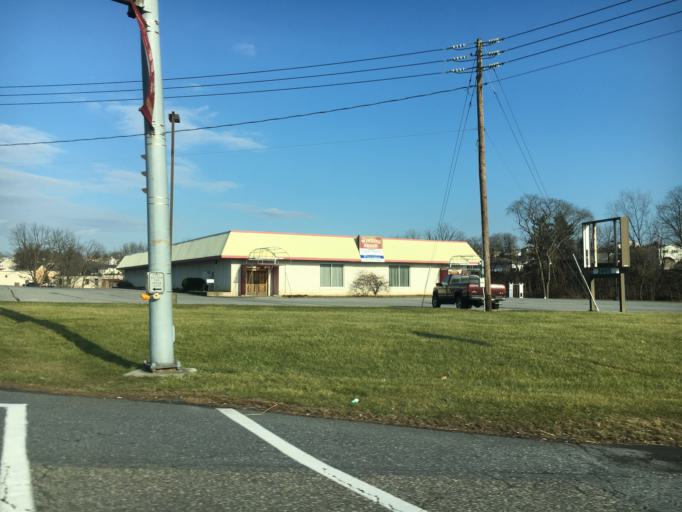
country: US
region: Pennsylvania
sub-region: Lehigh County
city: Stiles
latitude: 40.6653
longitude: -75.5118
